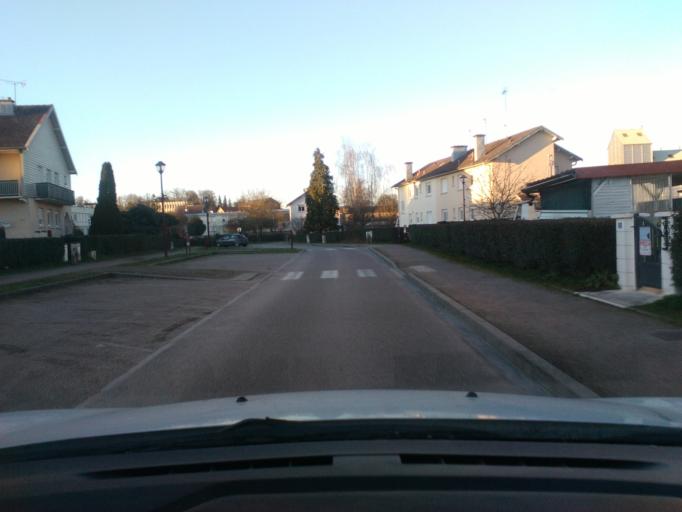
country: FR
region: Lorraine
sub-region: Departement des Vosges
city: Mirecourt
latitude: 48.2947
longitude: 6.1282
